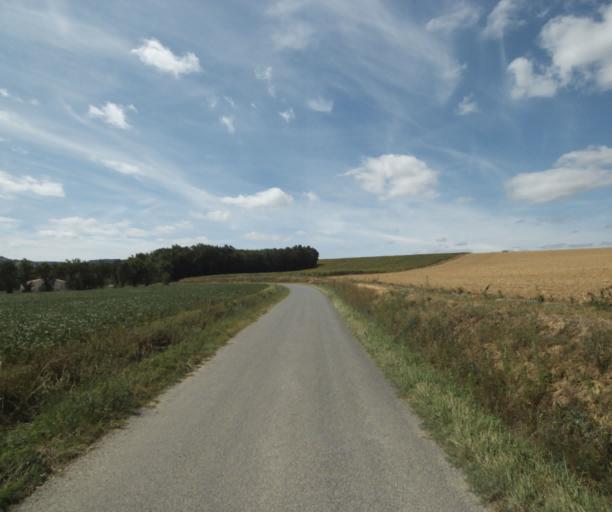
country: FR
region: Midi-Pyrenees
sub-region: Departement du Tarn
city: Soreze
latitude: 43.4780
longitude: 2.0761
